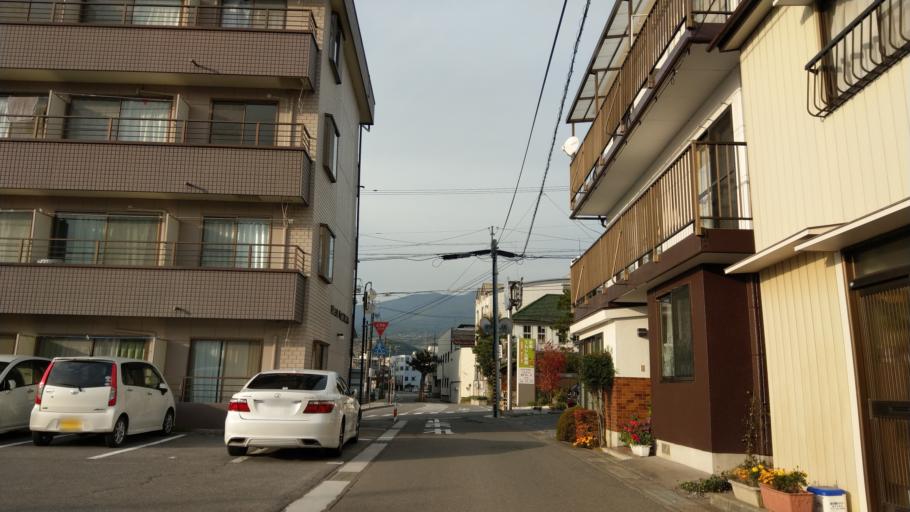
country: JP
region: Nagano
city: Komoro
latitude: 36.3254
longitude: 138.4265
